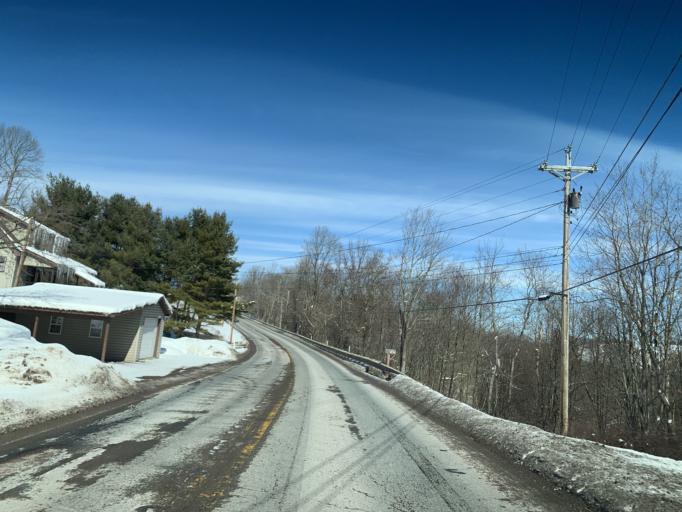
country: US
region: West Virginia
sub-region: Preston County
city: Terra Alta
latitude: 39.6706
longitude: -79.4512
